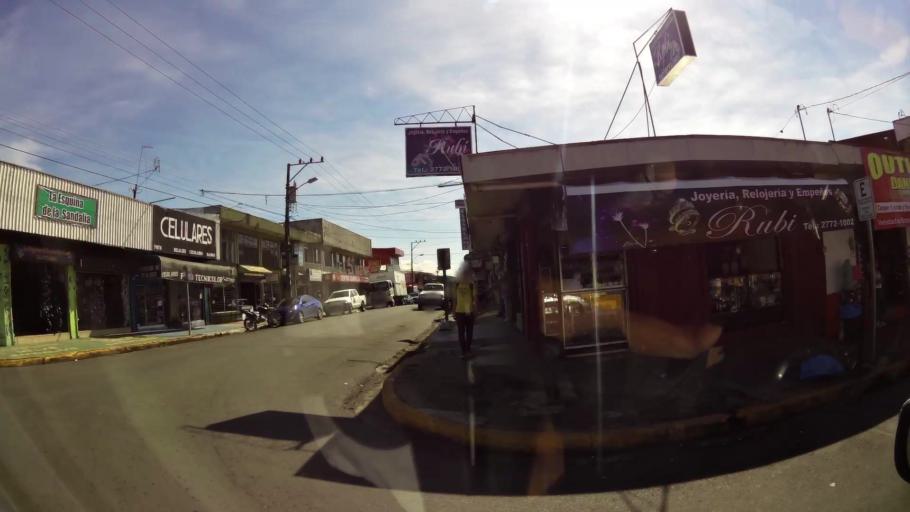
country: CR
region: San Jose
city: San Isidro
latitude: 9.3750
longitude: -83.7050
